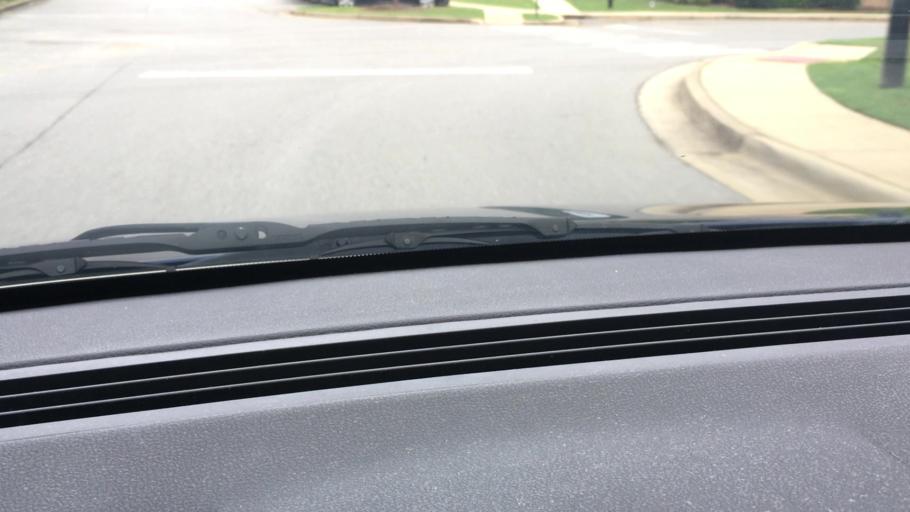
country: US
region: Alabama
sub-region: Tuscaloosa County
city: Tuscaloosa
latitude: 33.1905
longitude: -87.5189
